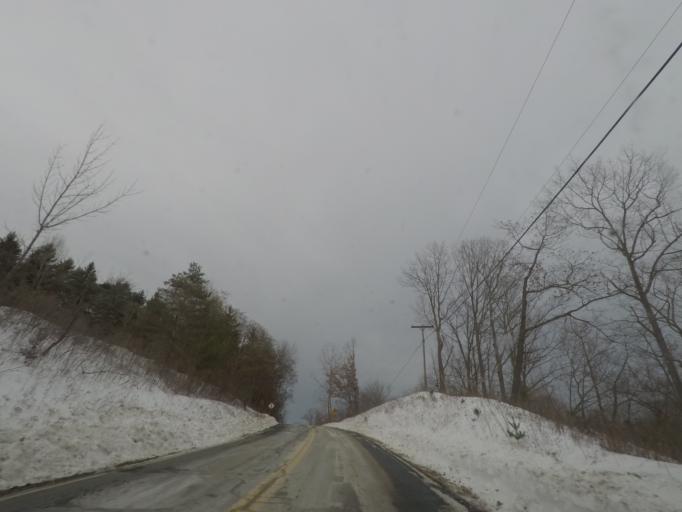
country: US
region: New York
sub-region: Rensselaer County
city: Castleton-on-Hudson
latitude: 42.5169
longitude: -73.7557
